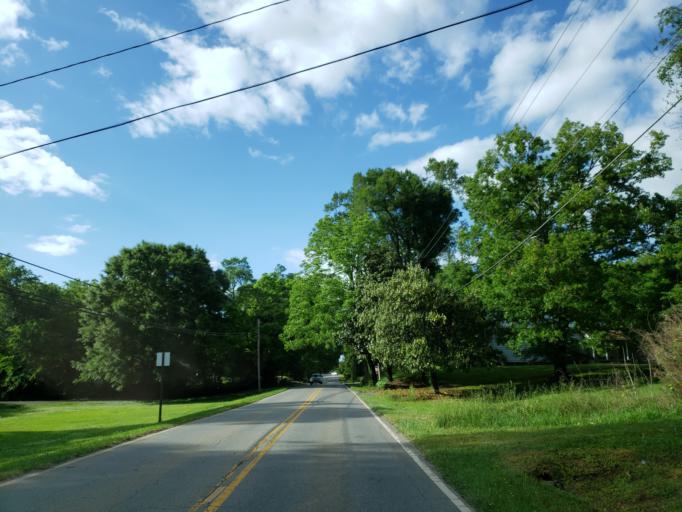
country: US
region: Georgia
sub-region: Bartow County
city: Cartersville
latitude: 34.2460
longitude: -84.8525
